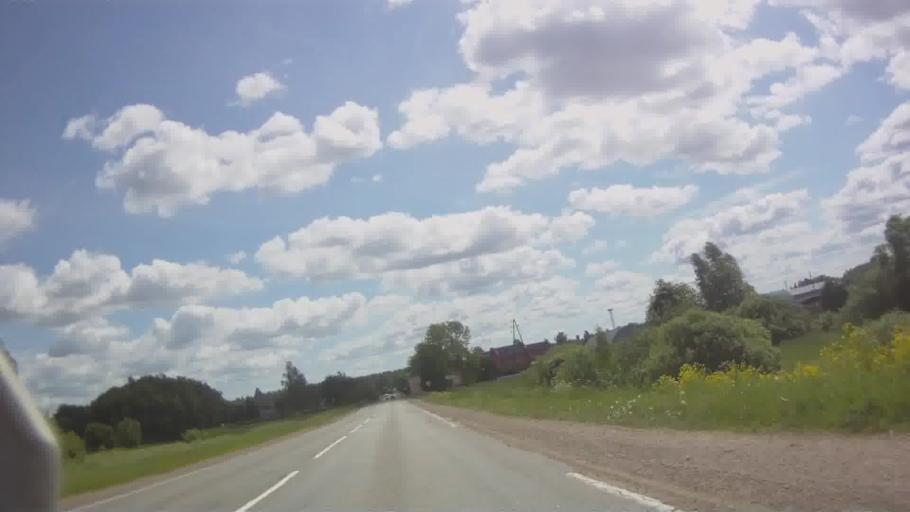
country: LV
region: Vilanu
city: Vilani
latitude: 56.5702
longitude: 26.9223
